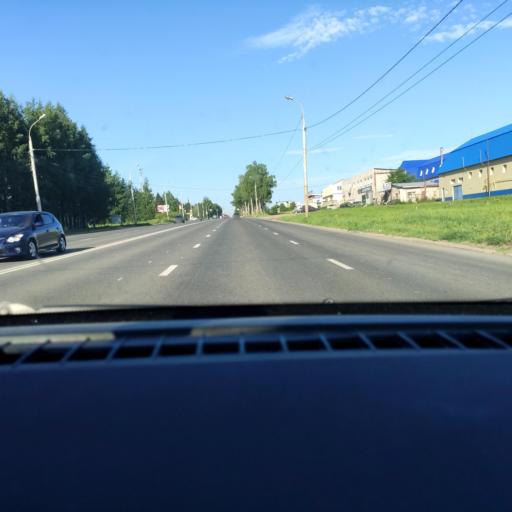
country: RU
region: Udmurtiya
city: Khokhryaki
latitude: 56.9036
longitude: 53.3319
